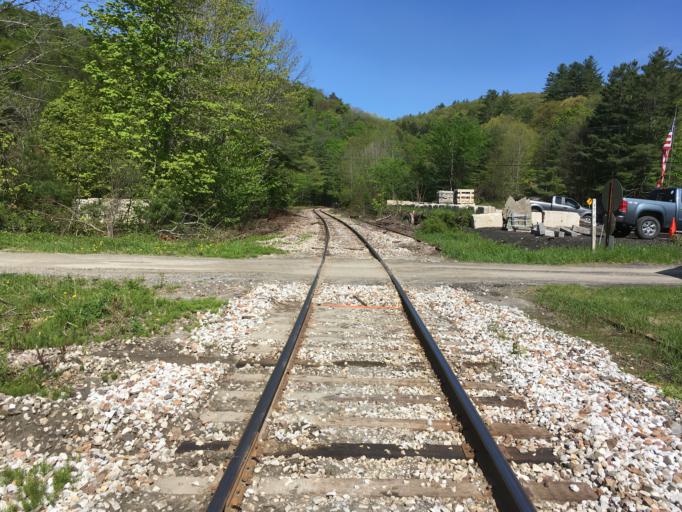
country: US
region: Vermont
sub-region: Windsor County
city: Chester
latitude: 43.3260
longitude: -72.6109
